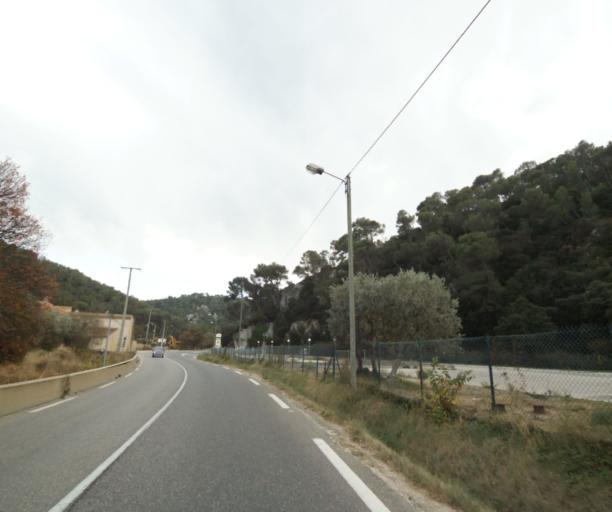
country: FR
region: Provence-Alpes-Cote d'Azur
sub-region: Departement des Bouches-du-Rhone
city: Gemenos
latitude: 43.2701
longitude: 5.6461
